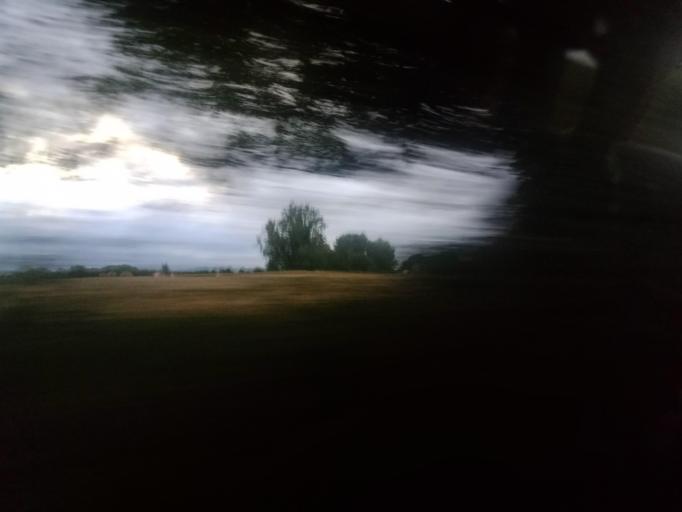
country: IE
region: Leinster
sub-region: Laois
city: Mountmellick
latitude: 53.1385
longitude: -7.3718
